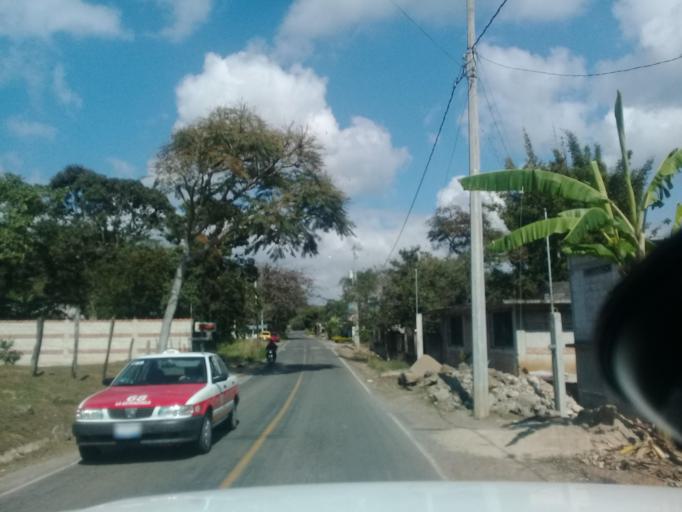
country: MX
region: Veracruz
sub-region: Coatepec
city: Bella Esperanza
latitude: 19.4364
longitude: -96.8682
